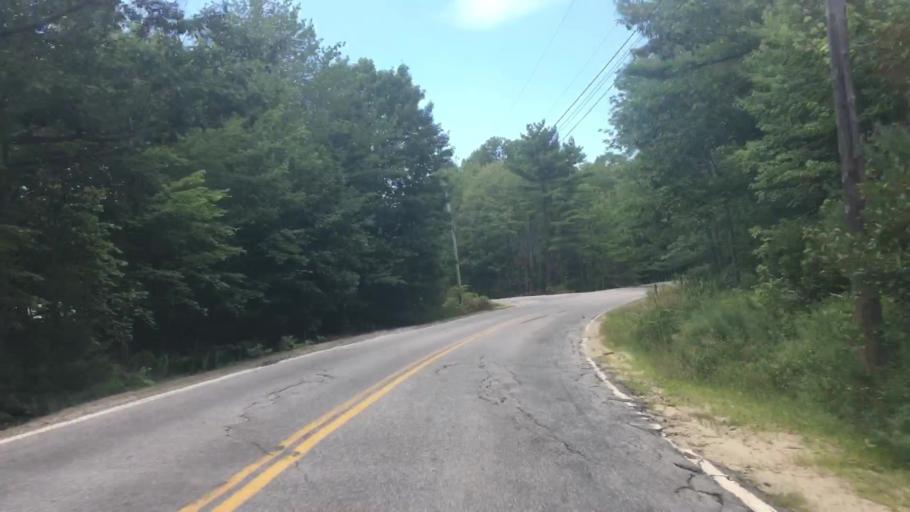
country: US
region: Maine
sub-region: Oxford County
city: Oxford
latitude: 44.0767
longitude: -70.5490
